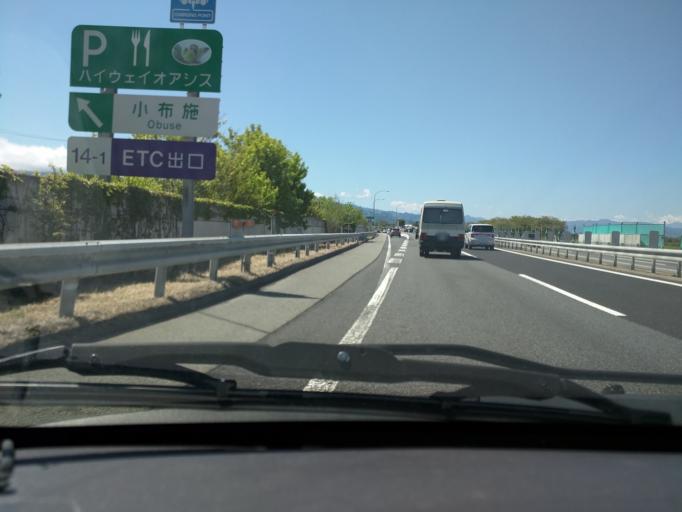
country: JP
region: Nagano
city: Suzaka
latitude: 36.6965
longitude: 138.2969
